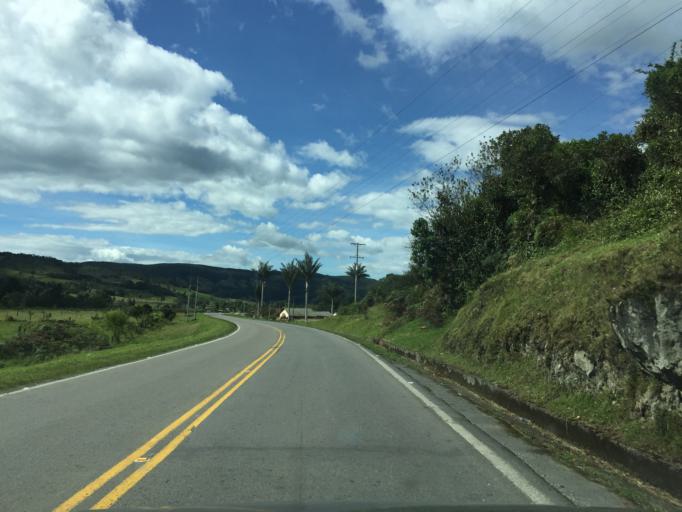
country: CO
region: Boyaca
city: Arcabuco
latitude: 5.7731
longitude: -73.4574
